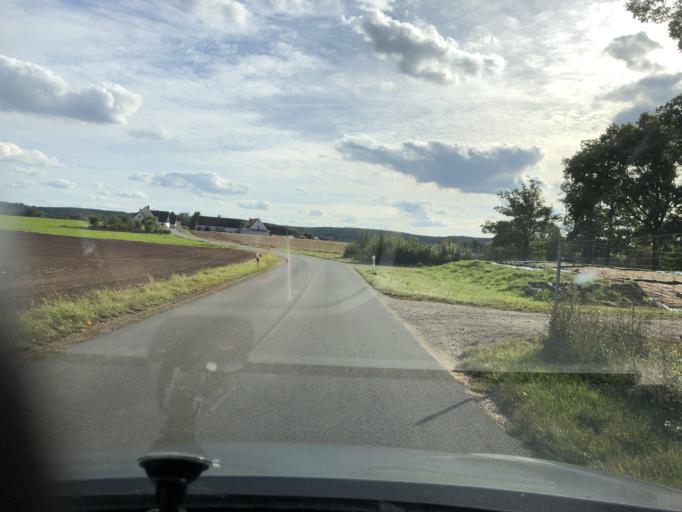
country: DE
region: Bavaria
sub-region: Regierungsbezirk Mittelfranken
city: Cadolzburg
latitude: 49.4777
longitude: 10.8250
